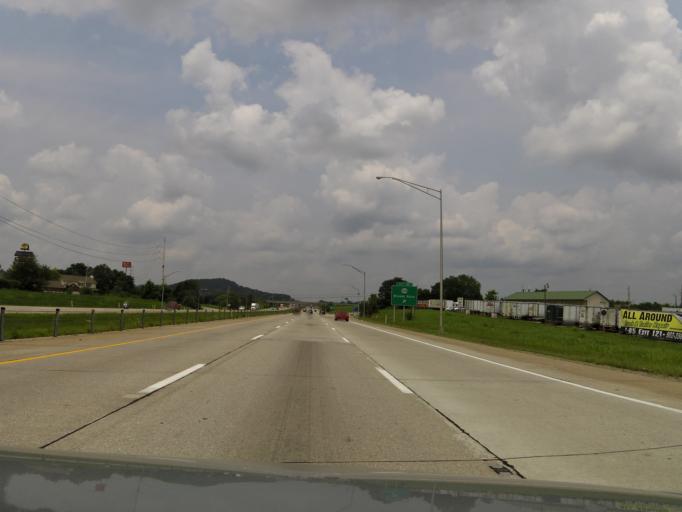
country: US
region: Kentucky
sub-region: Bullitt County
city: Brooks
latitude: 38.0577
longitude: -85.6987
